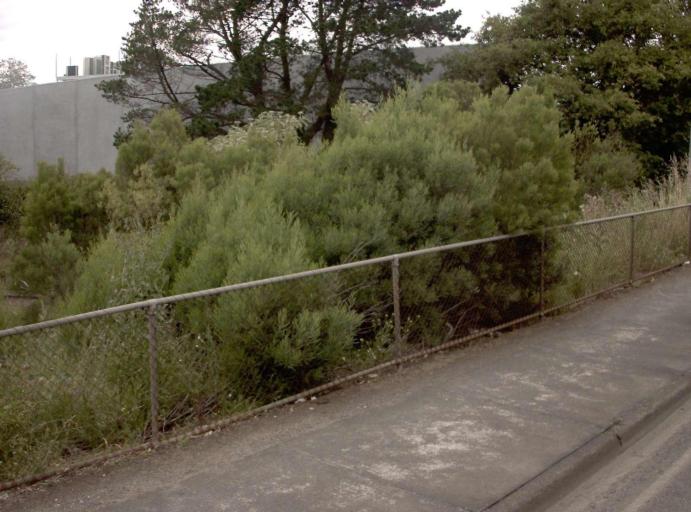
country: AU
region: Victoria
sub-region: Baw Baw
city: Warragul
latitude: -38.4795
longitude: 145.9481
